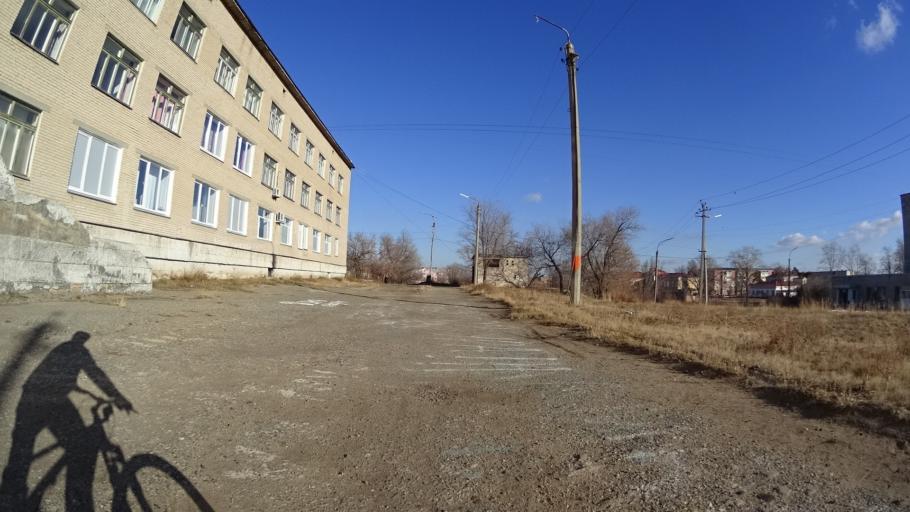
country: RU
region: Chelyabinsk
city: Troitsk
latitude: 54.0769
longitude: 61.5328
